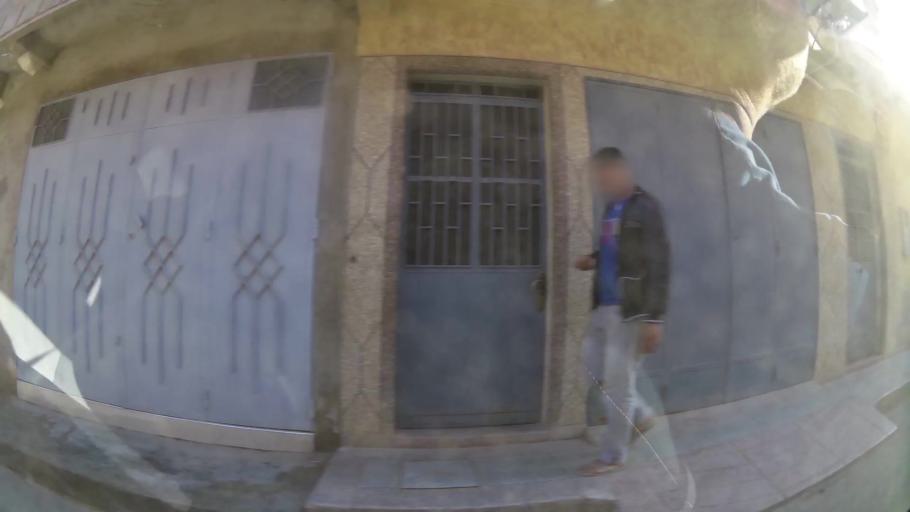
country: MA
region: Oriental
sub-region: Oujda-Angad
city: Oujda
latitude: 34.7103
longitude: -1.8974
